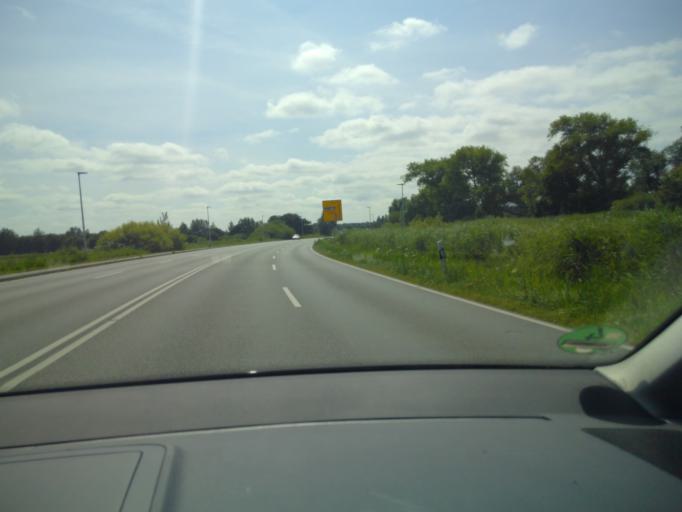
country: DE
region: Lower Saxony
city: Cuxhaven
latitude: 53.8323
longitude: 8.6807
